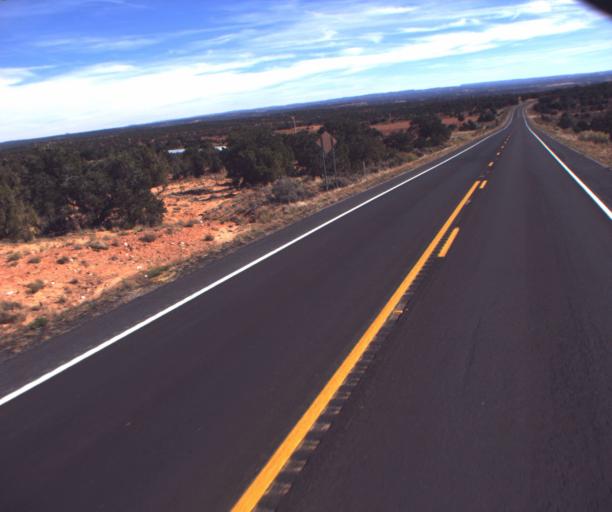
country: US
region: Arizona
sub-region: Coconino County
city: Kaibito
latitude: 36.5842
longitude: -110.8276
